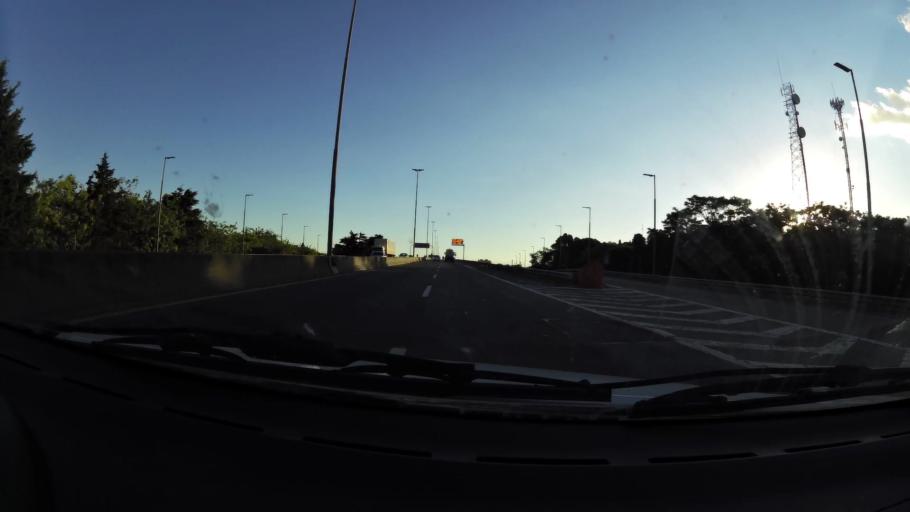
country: AR
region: Buenos Aires
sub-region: Partido de Quilmes
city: Quilmes
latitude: -34.7877
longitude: -58.1554
